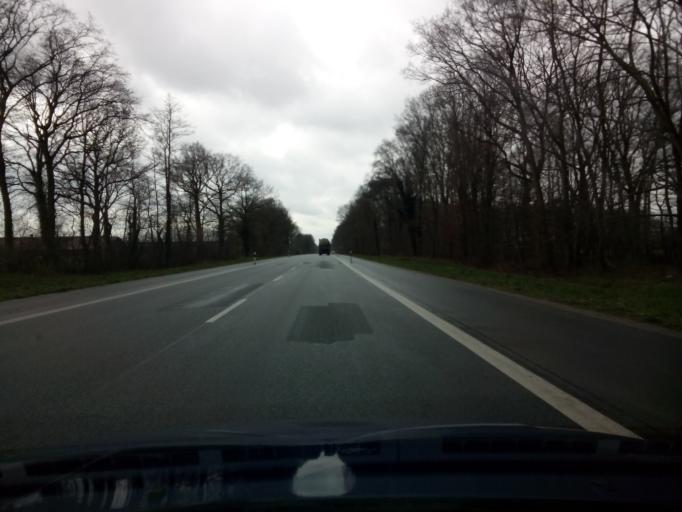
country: DE
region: Lower Saxony
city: Wildeshausen
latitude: 52.9414
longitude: 8.4762
